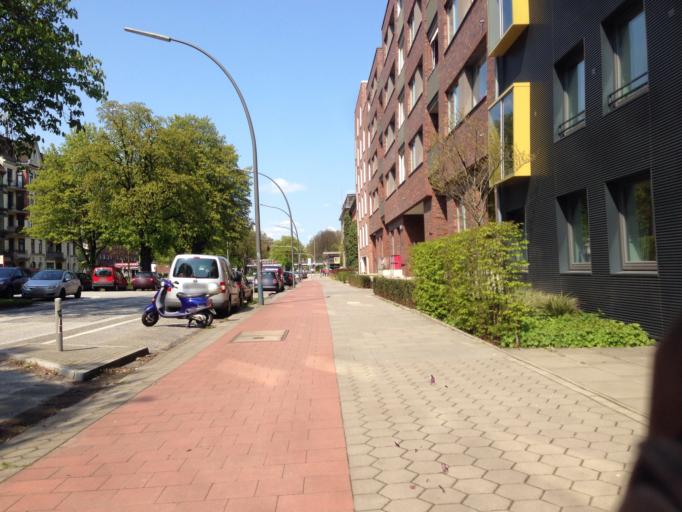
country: DE
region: Hamburg
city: Barmbek-Nord
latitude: 53.5860
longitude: 10.0338
